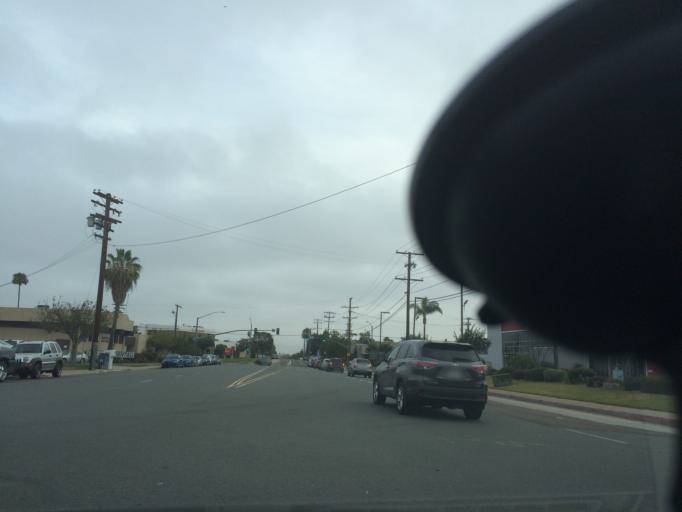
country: US
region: California
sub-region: San Diego County
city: San Diego
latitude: 32.8235
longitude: -117.1489
